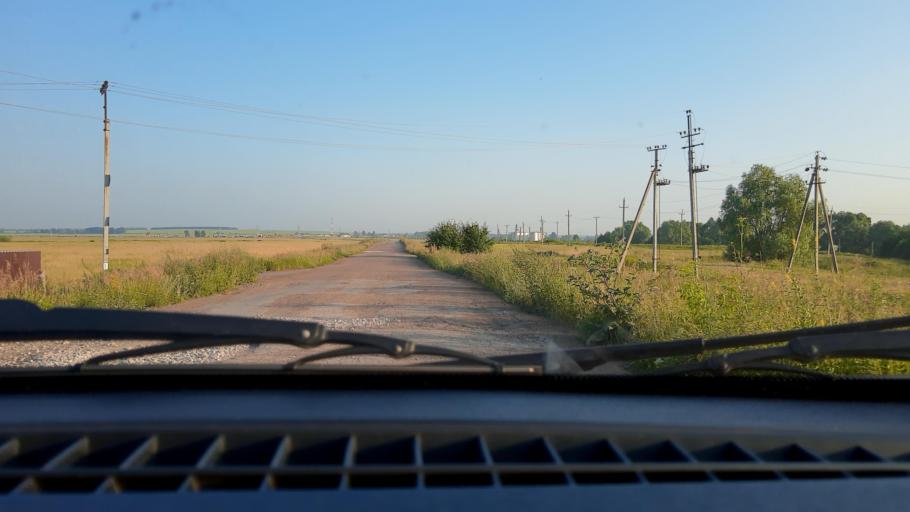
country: RU
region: Bashkortostan
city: Asanovo
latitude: 54.9143
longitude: 55.6272
